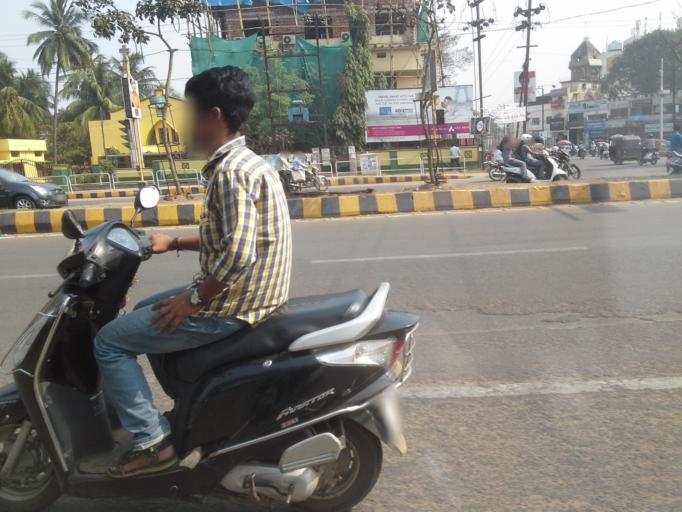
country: IN
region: Odisha
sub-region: Khordha
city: Bhubaneshwar
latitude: 20.2792
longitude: 85.8437
